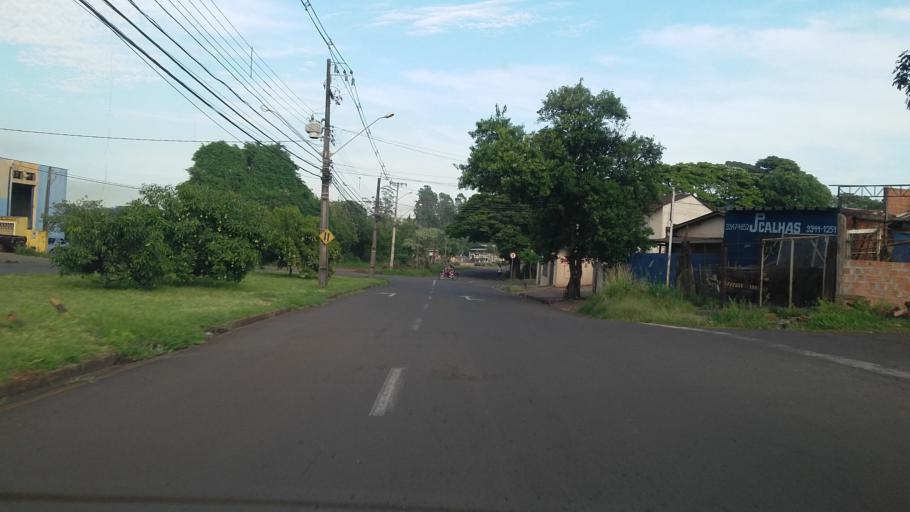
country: BR
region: Parana
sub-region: Londrina
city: Londrina
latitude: -23.2909
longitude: -51.2072
